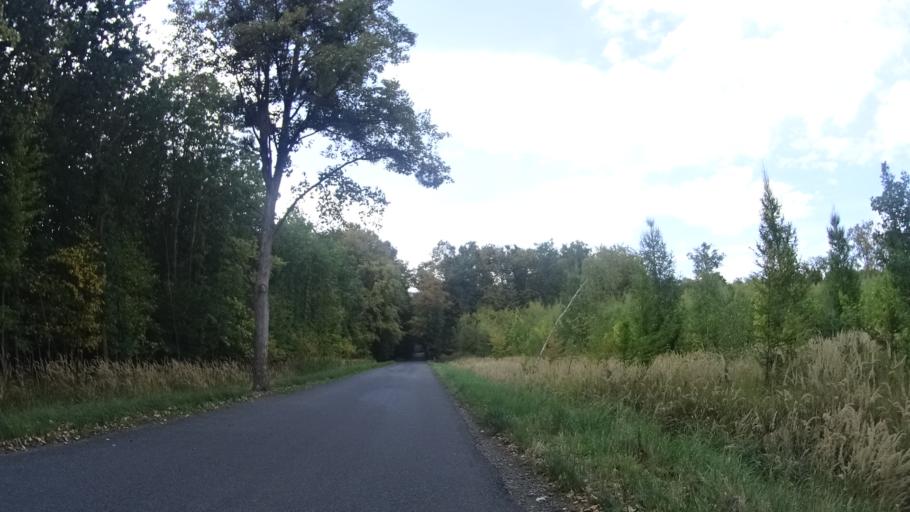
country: CZ
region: Olomoucky
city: Bila Lhota
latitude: 49.7278
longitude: 17.0146
